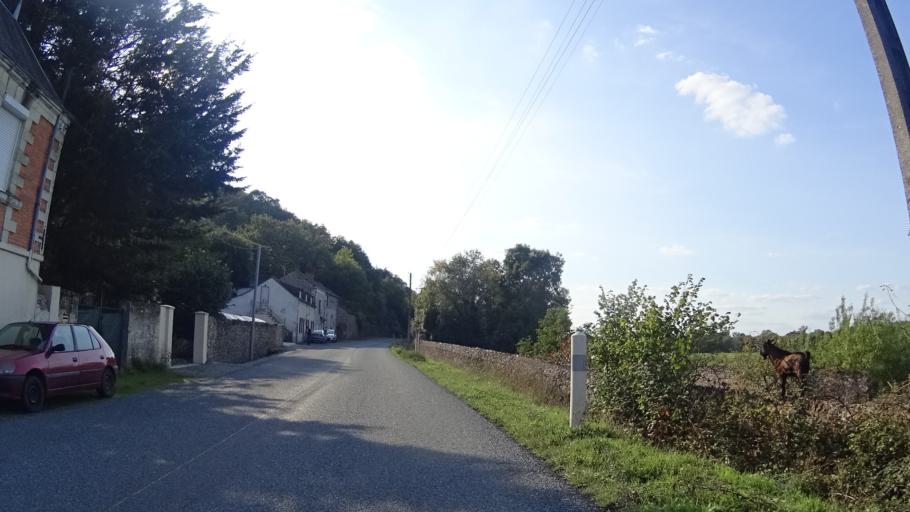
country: FR
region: Pays de la Loire
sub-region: Departement de Maine-et-Loire
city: Chalonnes-sur-Loire
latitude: 47.3475
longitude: -0.7231
